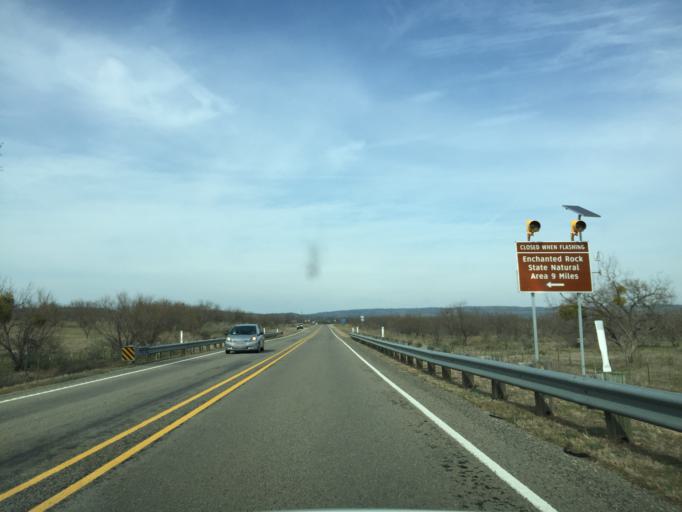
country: US
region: Texas
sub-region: Llano County
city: Llano
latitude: 30.5396
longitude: -98.7058
